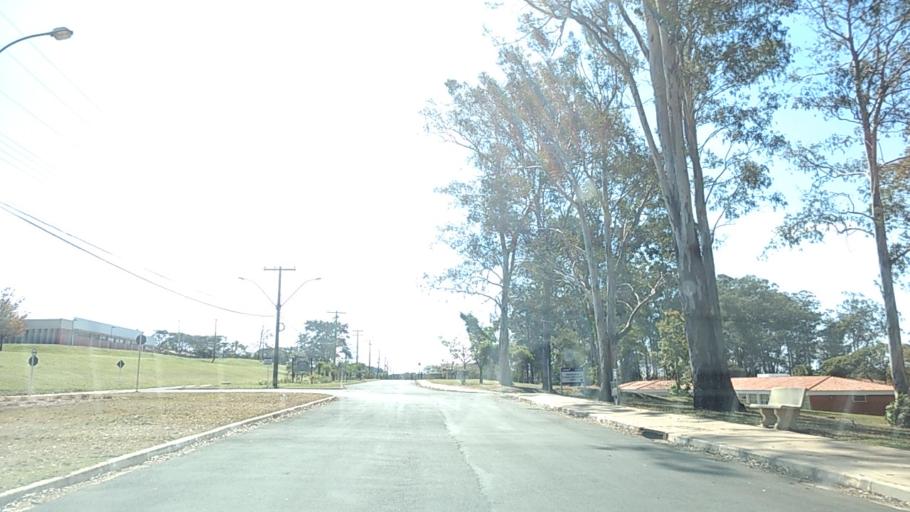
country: BR
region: Sao Paulo
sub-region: Botucatu
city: Botucatu
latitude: -22.8513
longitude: -48.4331
